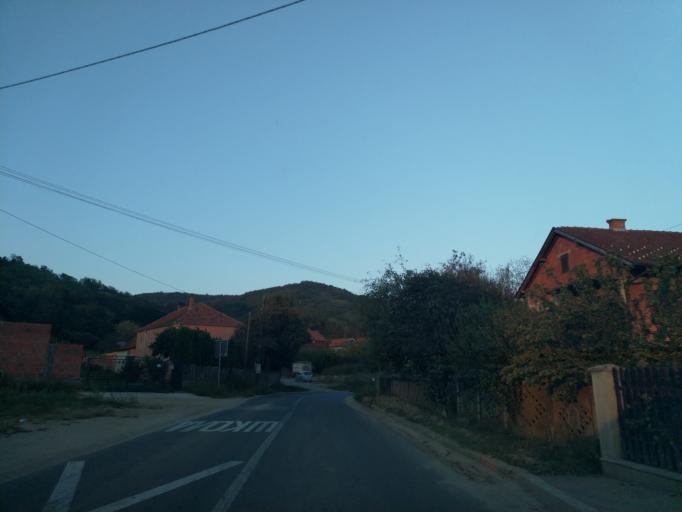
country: RS
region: Central Serbia
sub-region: Rasinski Okrug
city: Krusevac
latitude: 43.6048
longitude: 21.2392
